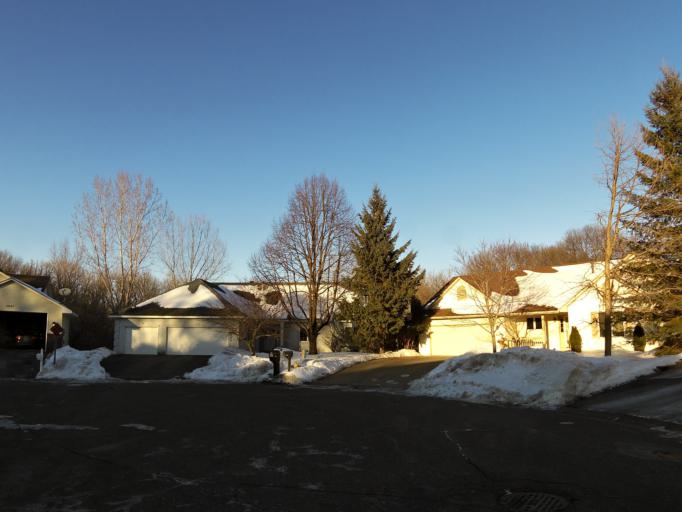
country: US
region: Minnesota
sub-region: Ramsey County
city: North Saint Paul
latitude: 45.0226
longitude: -93.0386
